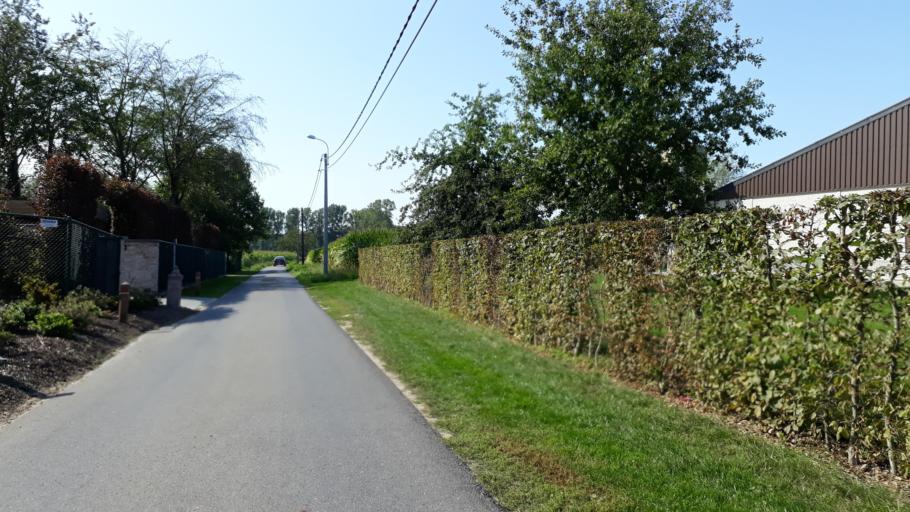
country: BE
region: Flanders
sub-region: Provincie West-Vlaanderen
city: Torhout
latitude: 51.0703
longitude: 3.0670
